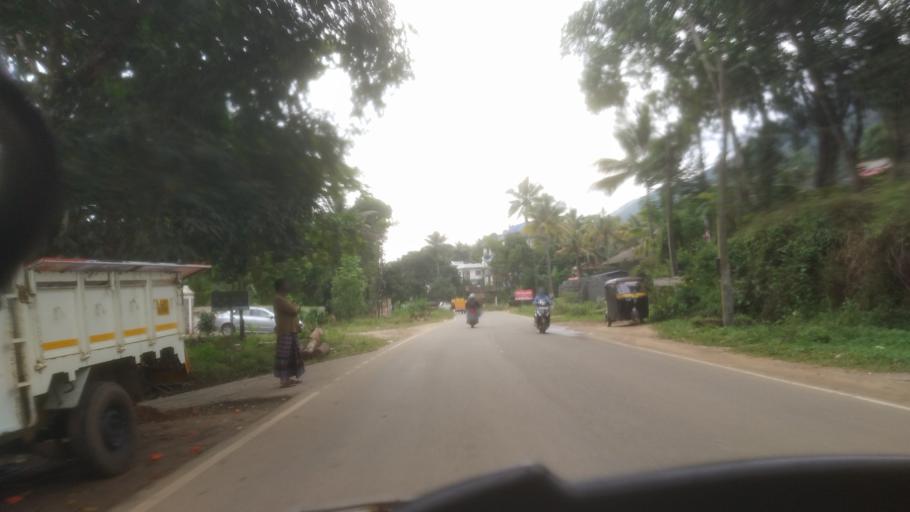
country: IN
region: Kerala
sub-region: Idukki
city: Munnar
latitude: 9.9971
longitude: 76.9738
